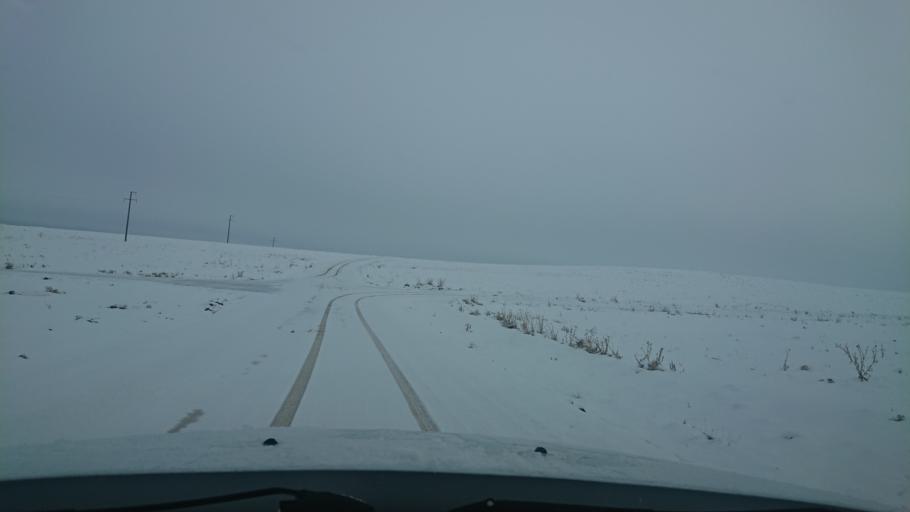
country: TR
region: Aksaray
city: Agacoren
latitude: 38.7376
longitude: 33.8697
